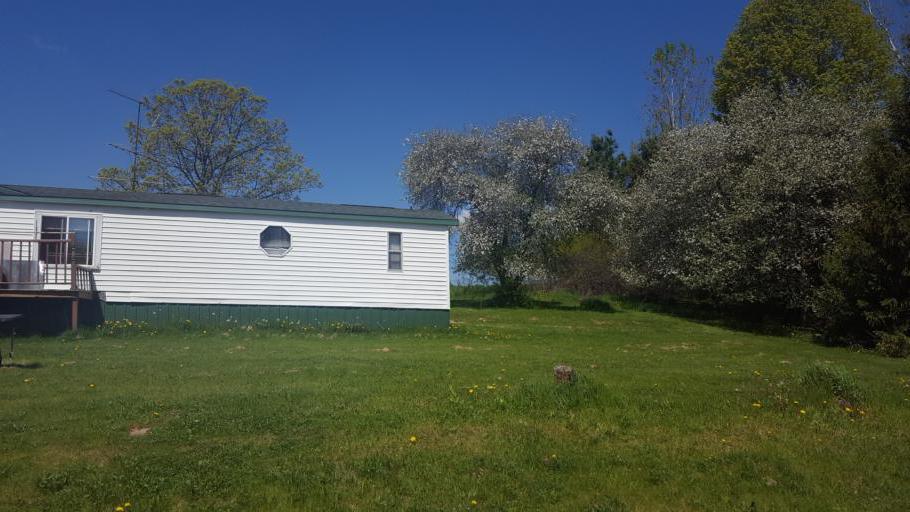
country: US
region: Wisconsin
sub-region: Vernon County
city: Hillsboro
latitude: 43.6401
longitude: -90.3682
